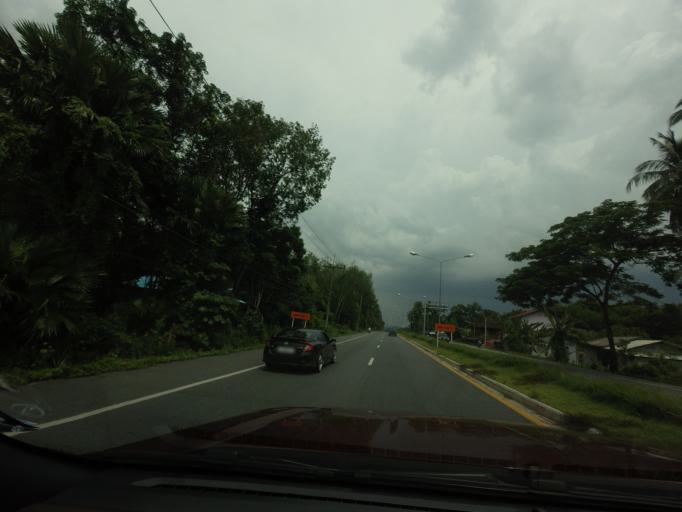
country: TH
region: Yala
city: Krong Pi Nang
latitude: 6.4588
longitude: 101.2738
